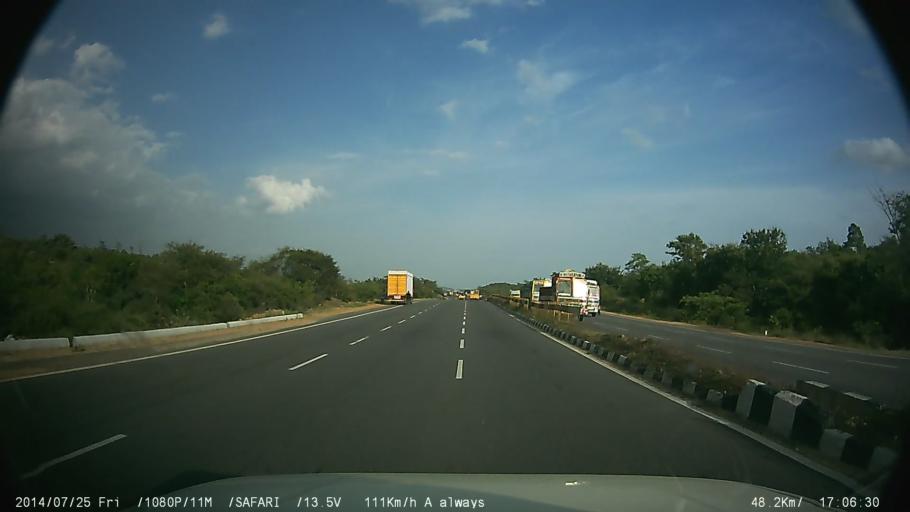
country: IN
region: Tamil Nadu
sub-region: Krishnagiri
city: Hosur
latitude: 12.7046
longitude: 77.9045
